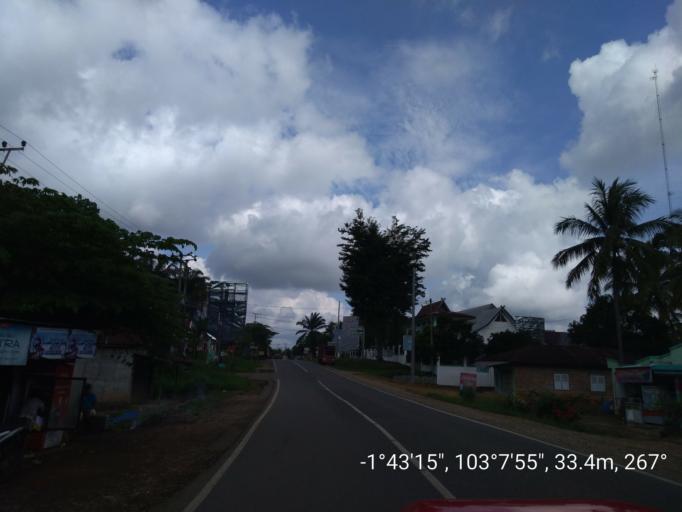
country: ID
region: Jambi
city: Muara Tembesi
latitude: -1.7210
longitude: 103.1322
